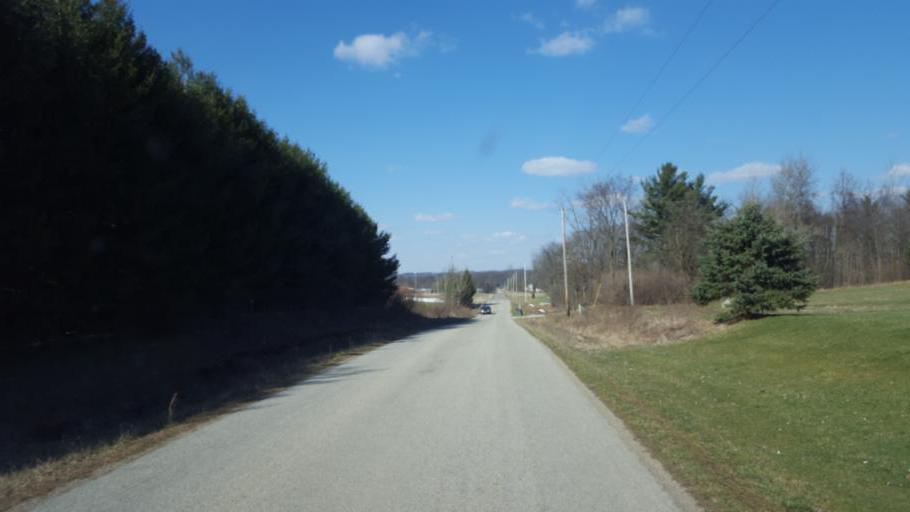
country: US
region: Ohio
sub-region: Knox County
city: Fredericktown
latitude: 40.4457
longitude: -82.6781
